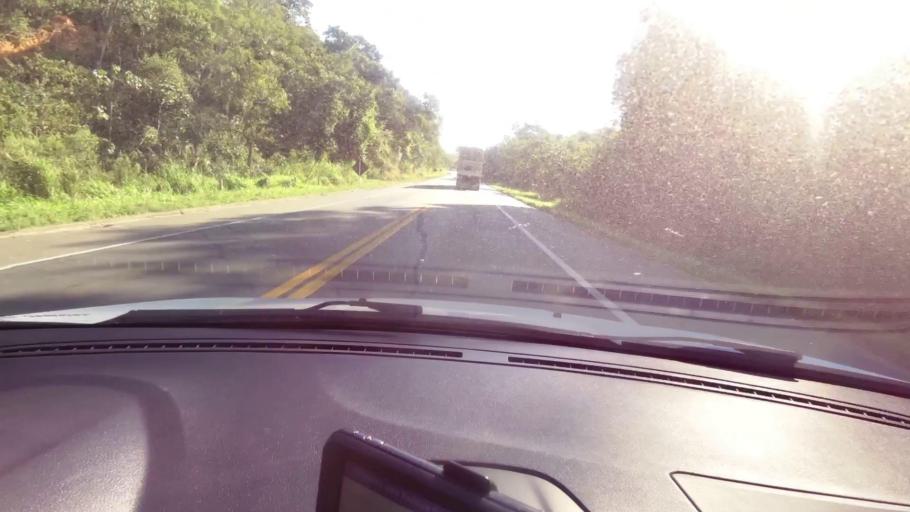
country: BR
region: Espirito Santo
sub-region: Alfredo Chaves
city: Alfredo Chaves
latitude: -20.6657
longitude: -40.6567
